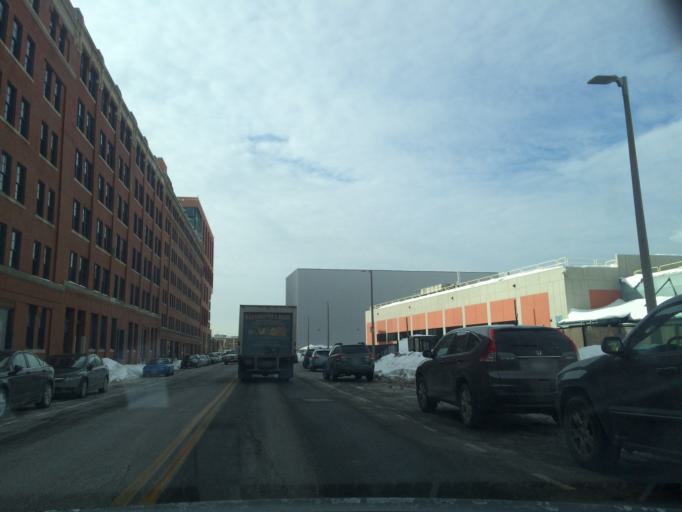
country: US
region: Massachusetts
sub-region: Suffolk County
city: South Boston
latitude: 42.3467
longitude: -71.0514
